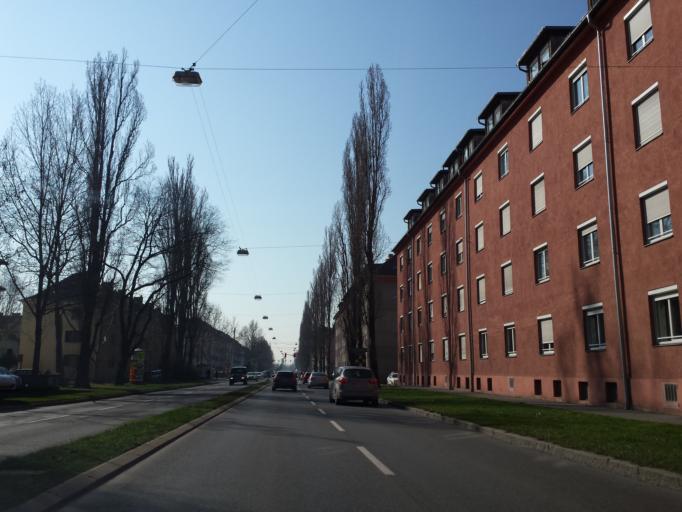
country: AT
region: Styria
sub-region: Graz Stadt
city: Graz
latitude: 47.0533
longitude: 15.4280
